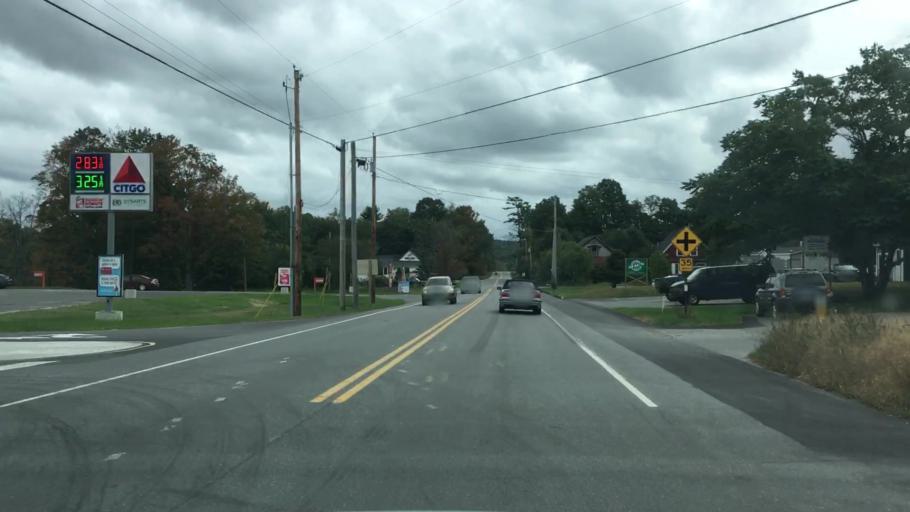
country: US
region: Maine
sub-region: Penobscot County
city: Hermon
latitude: 44.7568
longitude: -68.9737
